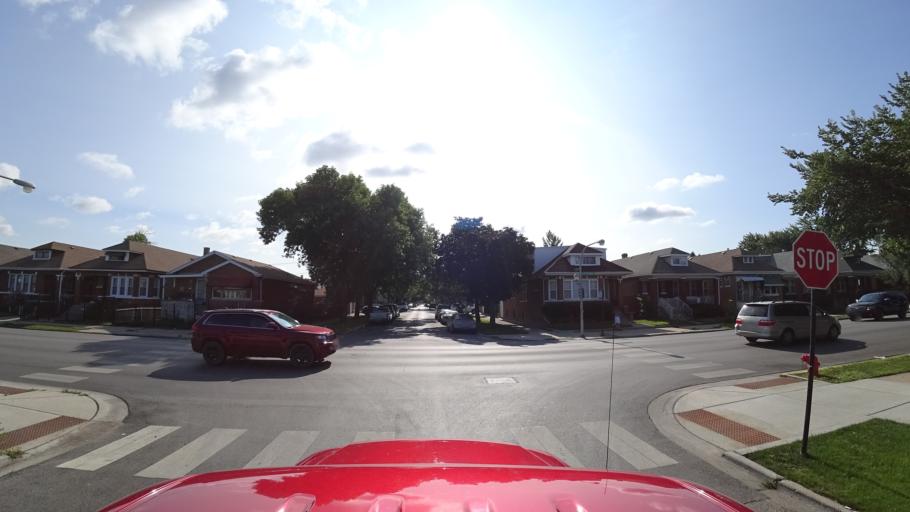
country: US
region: Illinois
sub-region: Cook County
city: Hometown
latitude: 41.7919
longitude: -87.6940
